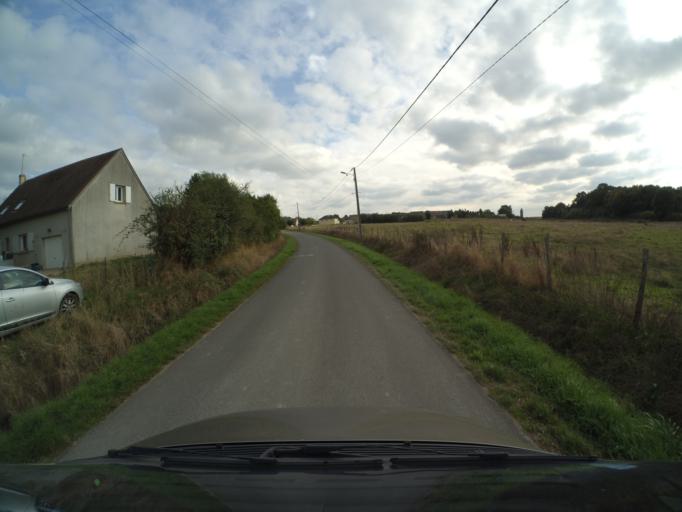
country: FR
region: Centre
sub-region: Departement d'Indre-et-Loire
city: Poce-sur-Cisse
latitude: 47.4750
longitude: 0.9649
